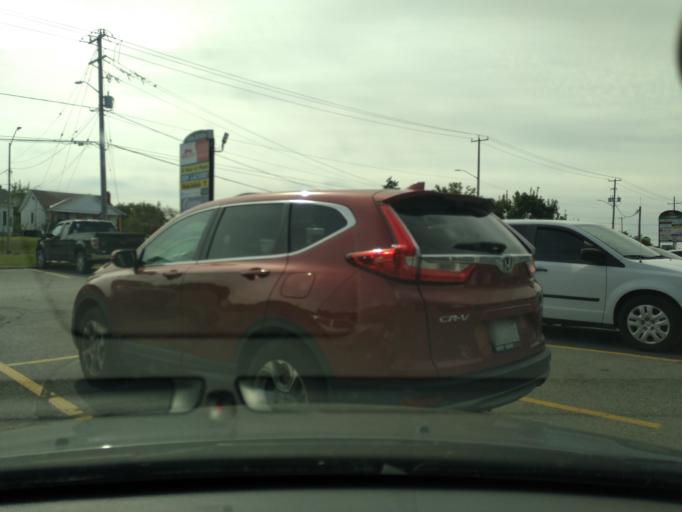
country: CA
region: Ontario
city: Oshawa
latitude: 43.8896
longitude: -78.9012
